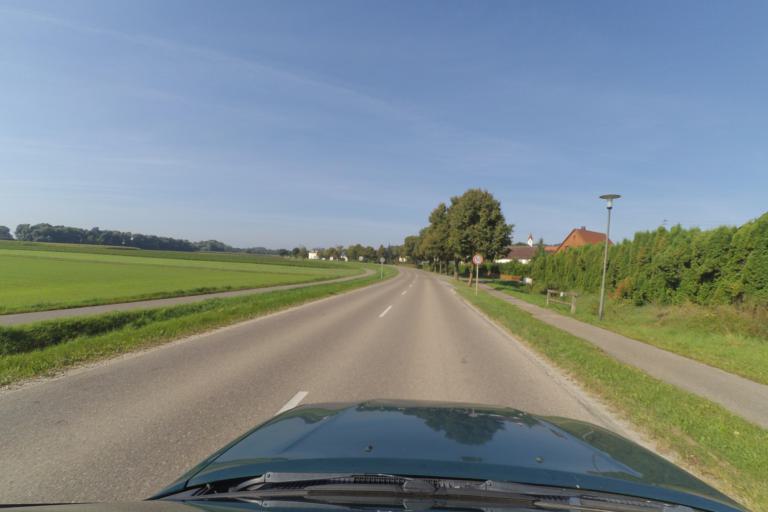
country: DE
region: Bavaria
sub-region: Swabia
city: Donauwoerth
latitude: 48.7204
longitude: 10.8142
